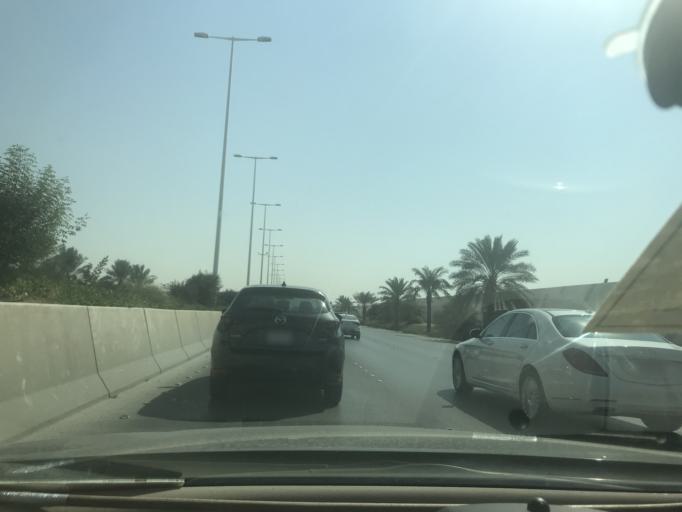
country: SA
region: Ar Riyad
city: Riyadh
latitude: 24.7218
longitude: 46.7118
